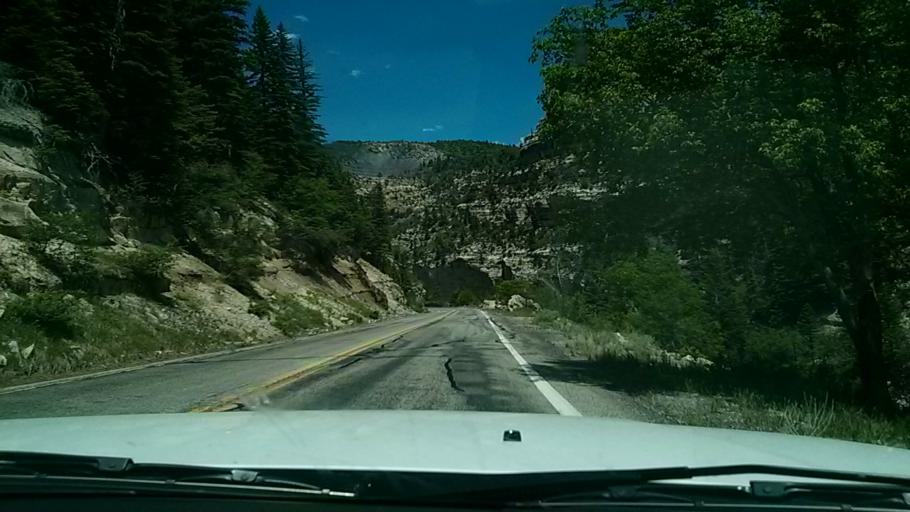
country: US
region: Utah
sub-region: Iron County
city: Cedar City
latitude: 37.6231
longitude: -112.9331
